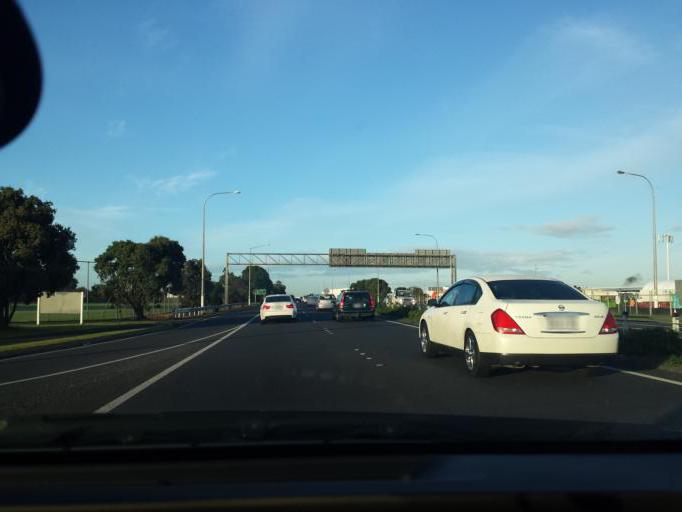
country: NZ
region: Auckland
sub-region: Auckland
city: Mangere
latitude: -36.9739
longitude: 174.7893
